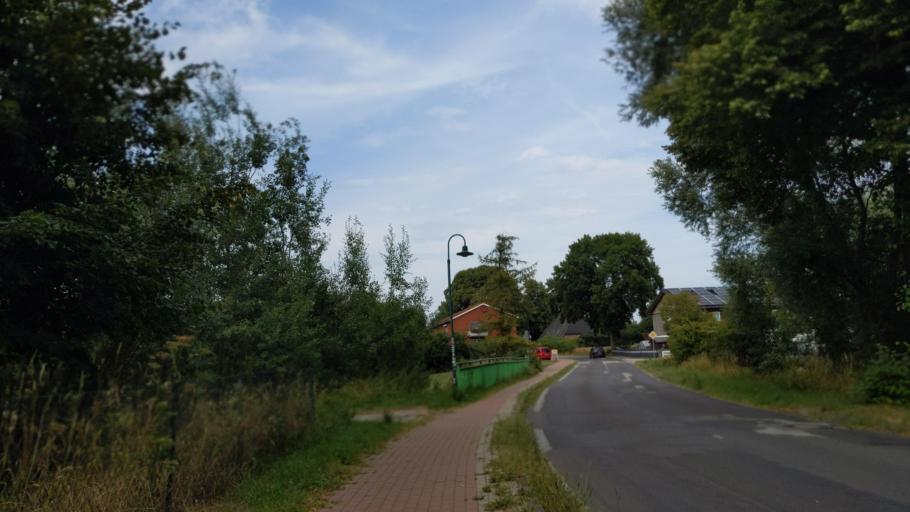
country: DE
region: Schleswig-Holstein
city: Gross Gronau
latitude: 53.8301
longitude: 10.8101
